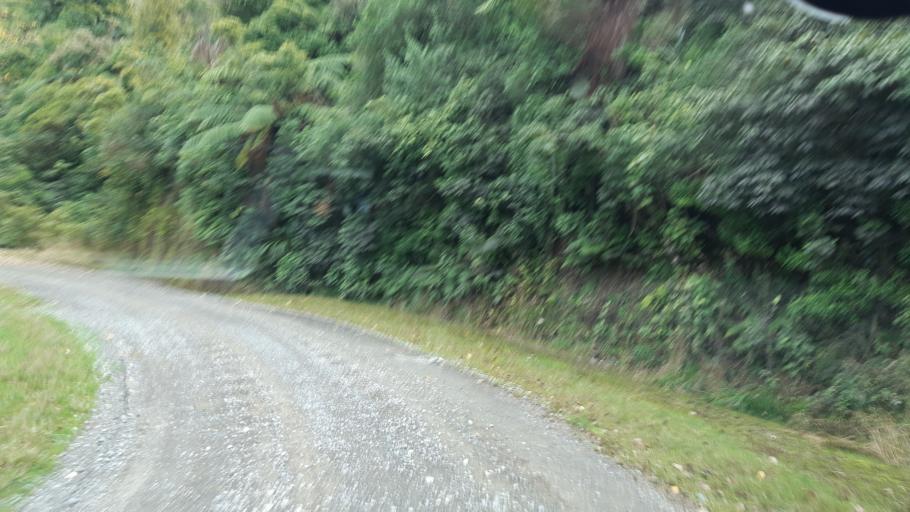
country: NZ
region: Manawatu-Wanganui
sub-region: Ruapehu District
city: Waiouru
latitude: -39.7934
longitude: 175.6741
